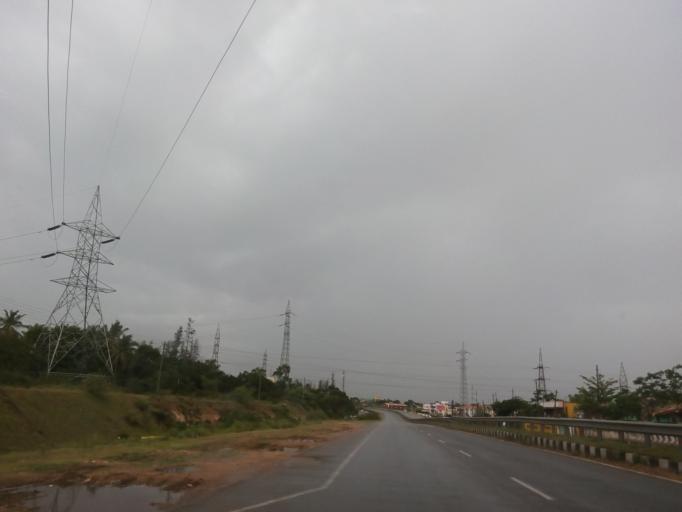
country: IN
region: Karnataka
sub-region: Davanagere
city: Harihar
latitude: 14.4314
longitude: 75.9221
